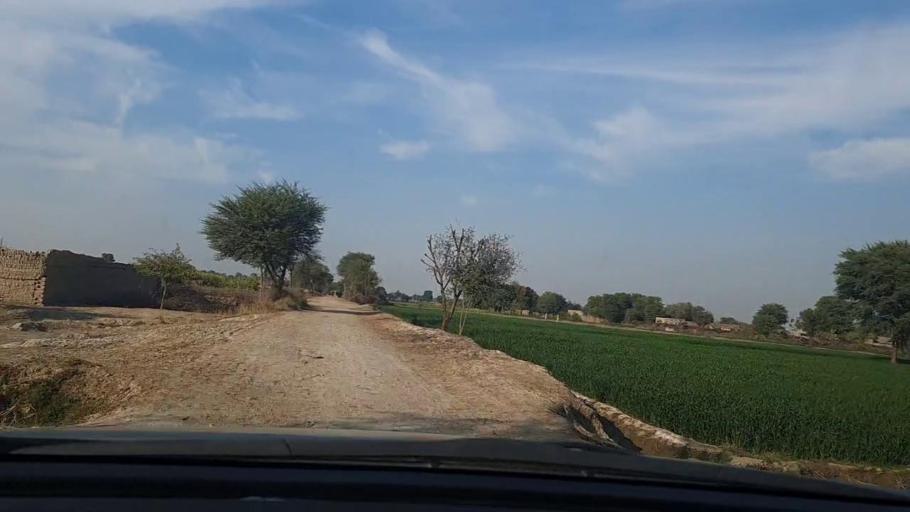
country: PK
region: Sindh
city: Sehwan
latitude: 26.3123
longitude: 68.0204
